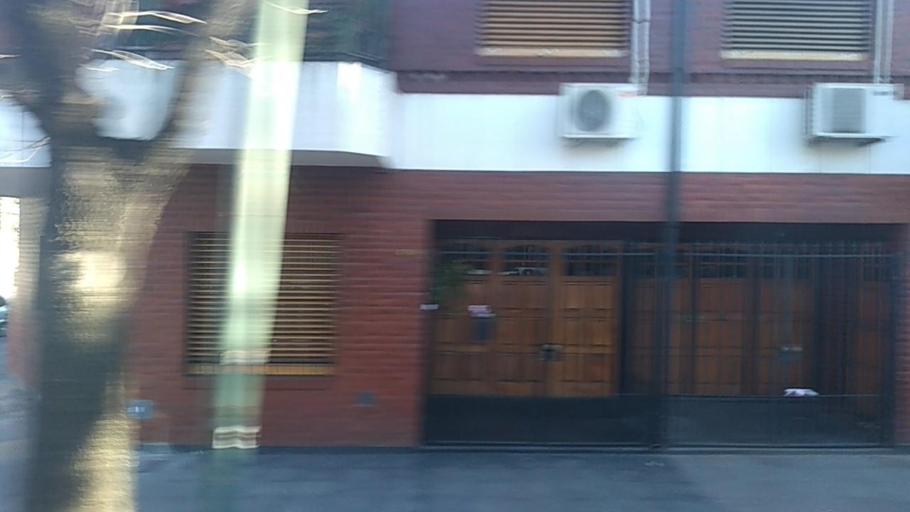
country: AR
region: Buenos Aires F.D.
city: Villa Santa Rita
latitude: -34.6251
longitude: -58.5005
